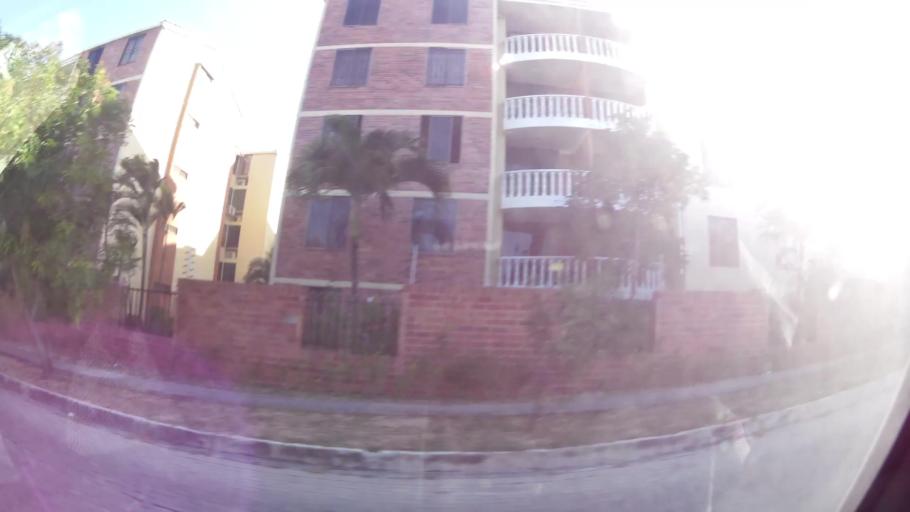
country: CO
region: Atlantico
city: Barranquilla
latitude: 11.0008
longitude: -74.8338
